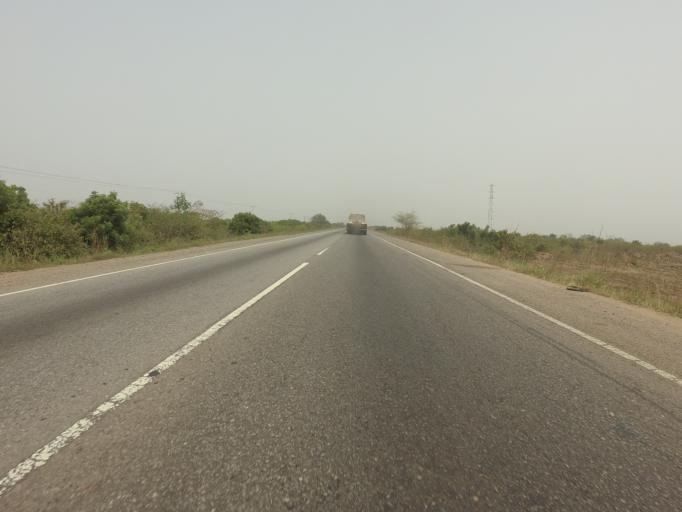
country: GH
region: Greater Accra
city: Tema
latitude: 5.7812
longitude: 0.0942
